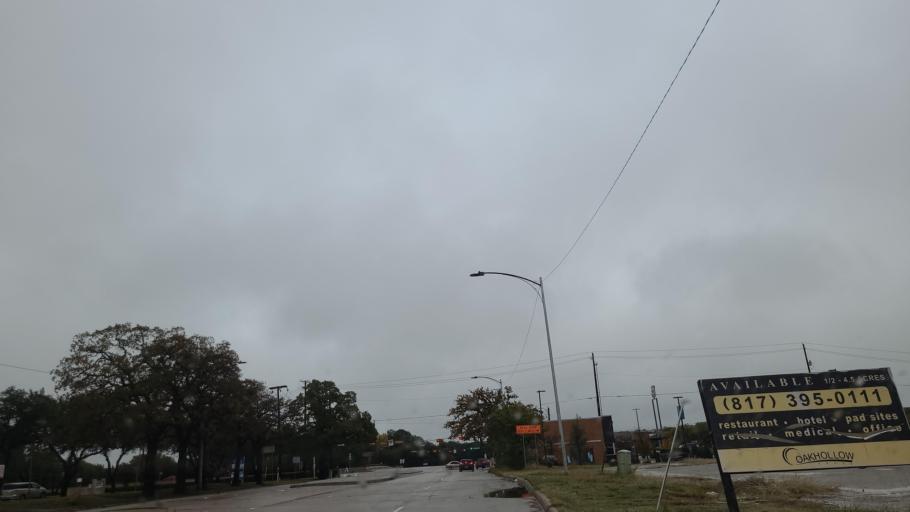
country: US
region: Texas
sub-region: Tarrant County
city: Arlington
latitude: 32.7672
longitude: -97.0651
